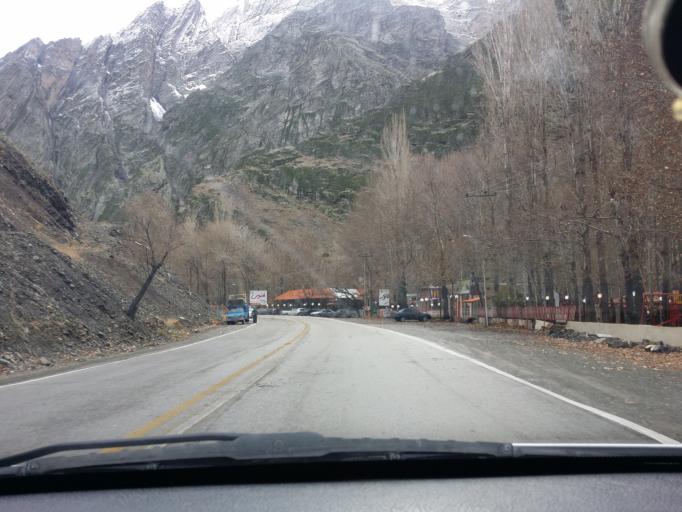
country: IR
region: Tehran
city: Tajrish
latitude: 36.0204
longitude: 51.2673
